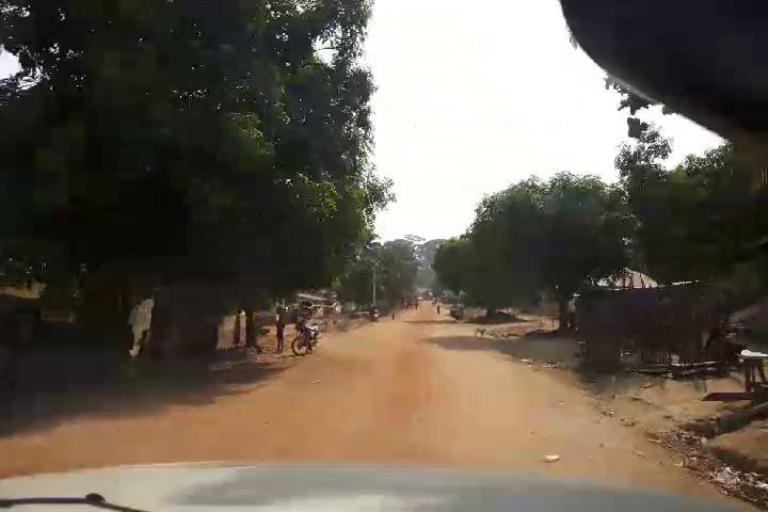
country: SL
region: Northern Province
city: Masingbi
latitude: 8.8606
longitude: -11.8137
